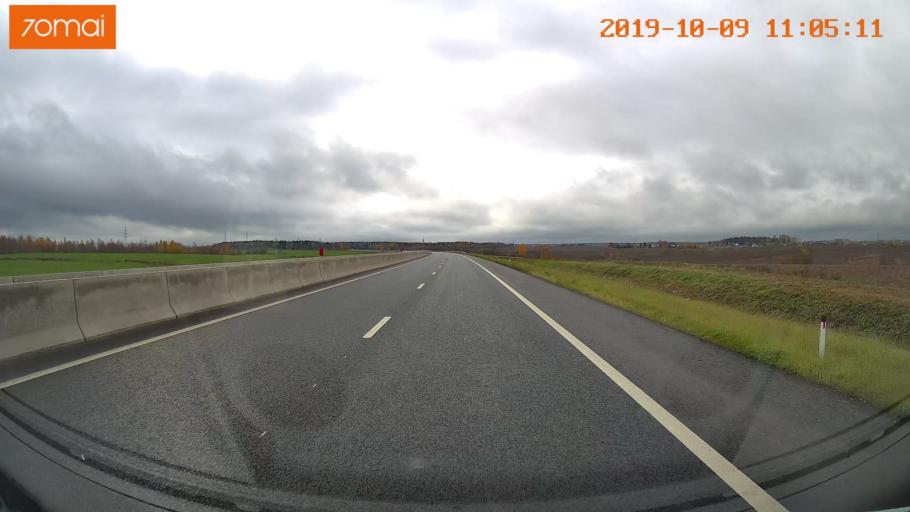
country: RU
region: Vologda
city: Molochnoye
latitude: 59.2033
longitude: 39.7596
